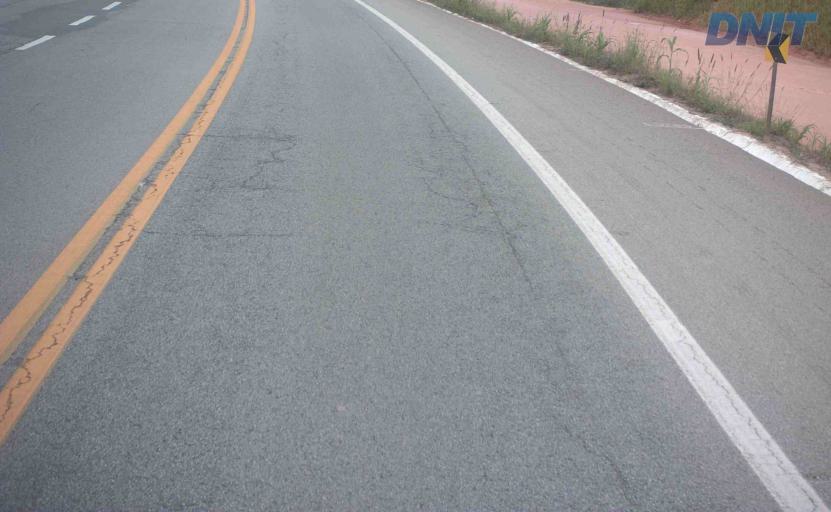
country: BR
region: Minas Gerais
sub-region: Barao De Cocais
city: Barao de Cocais
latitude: -19.7600
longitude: -43.4624
